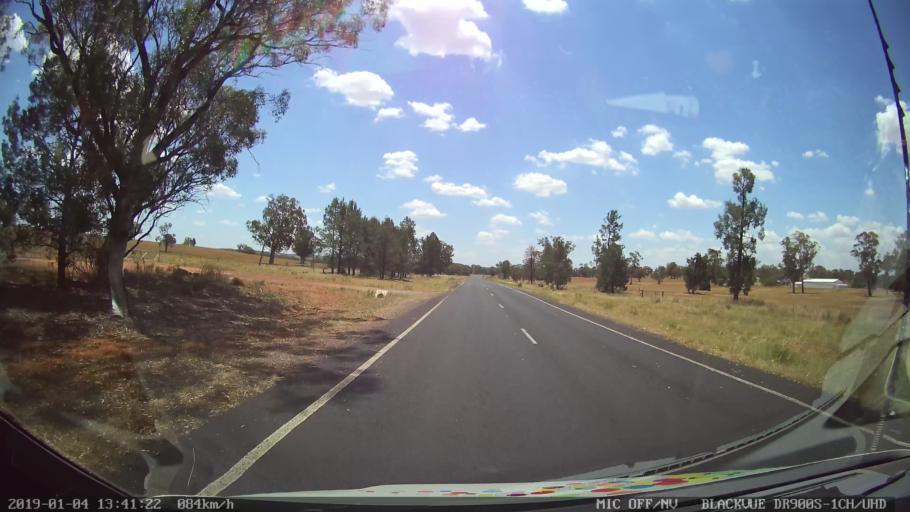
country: AU
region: New South Wales
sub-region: Dubbo Municipality
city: Dubbo
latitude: -32.5031
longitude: 148.5536
